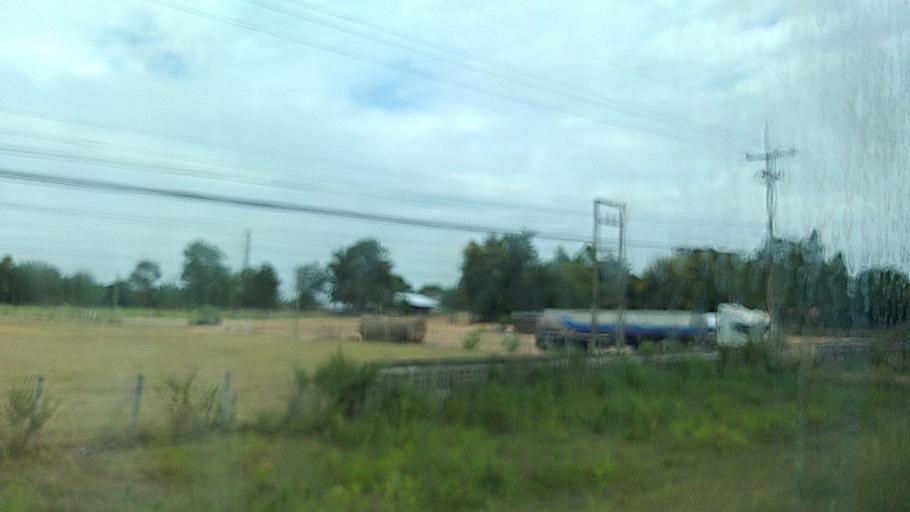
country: TH
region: Roi Et
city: Changhan
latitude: 16.1210
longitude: 103.4846
